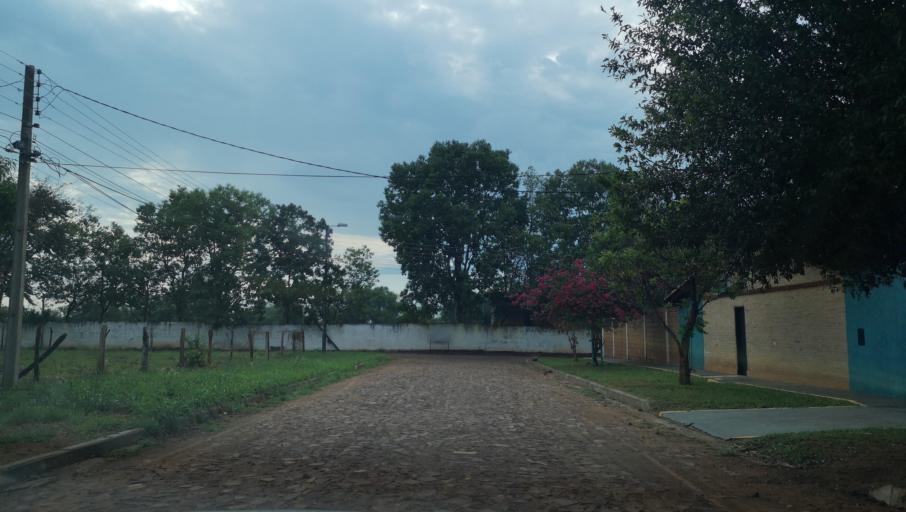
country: PY
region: Misiones
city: Santa Maria
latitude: -26.8794
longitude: -57.0295
